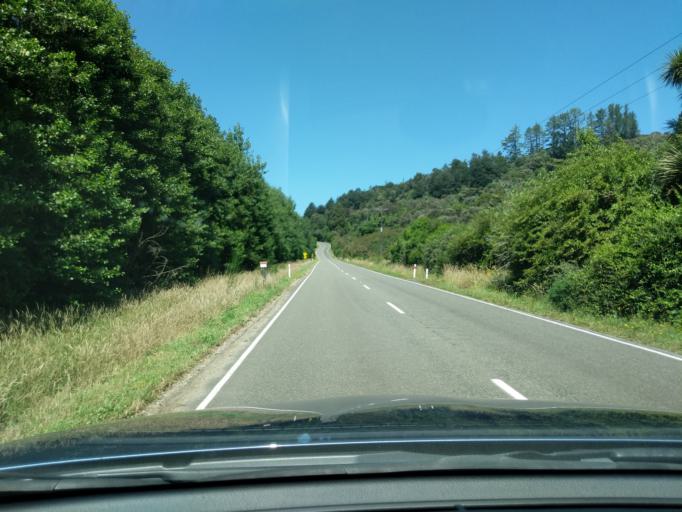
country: NZ
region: Tasman
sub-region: Tasman District
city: Takaka
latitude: -40.7230
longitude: 172.6013
